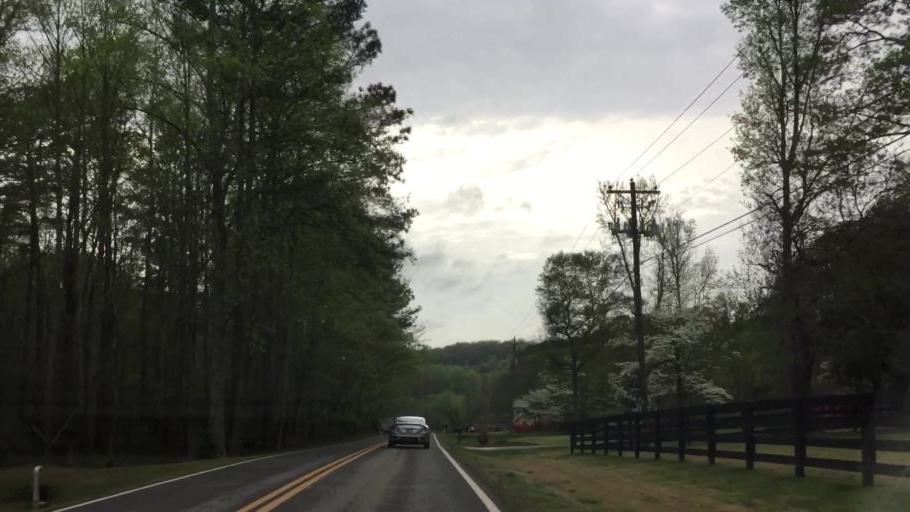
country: US
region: Georgia
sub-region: Fulton County
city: Milton
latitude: 34.1992
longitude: -84.3643
